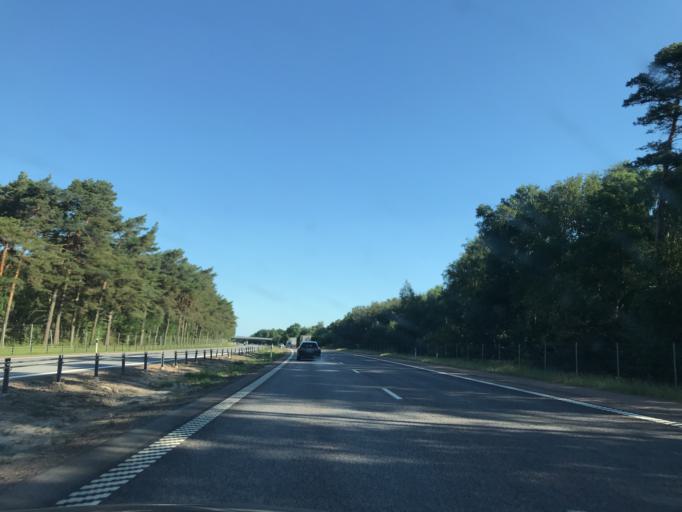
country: SE
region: Halland
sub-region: Halmstads Kommun
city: Paarp
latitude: 56.5829
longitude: 12.9471
